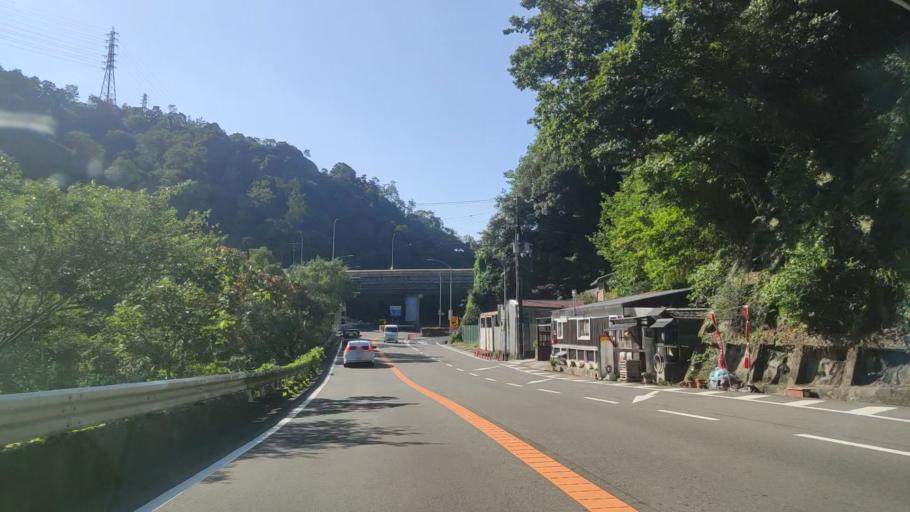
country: JP
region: Hyogo
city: Kobe
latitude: 34.7005
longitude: 135.1649
